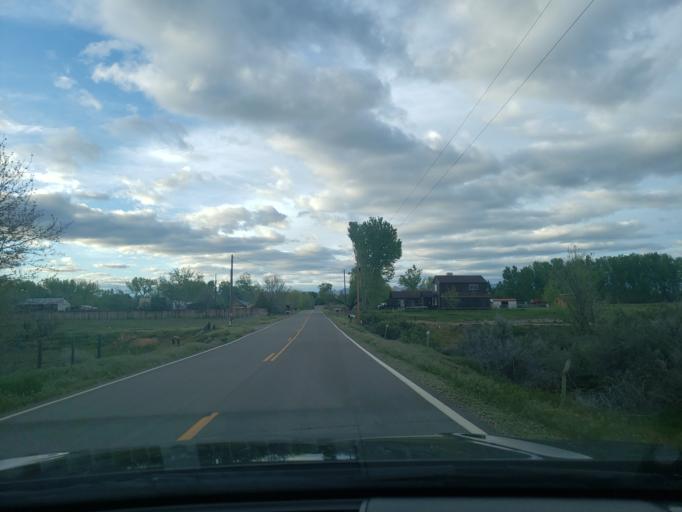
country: US
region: Colorado
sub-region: Mesa County
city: Fruita
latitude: 39.2052
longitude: -108.7291
